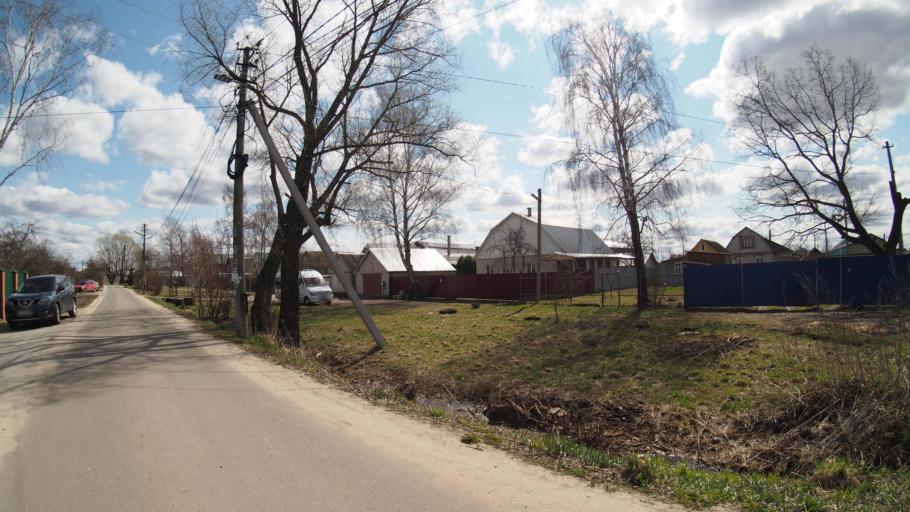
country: RU
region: Moskovskaya
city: Malyshevo
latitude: 55.5318
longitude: 38.3316
